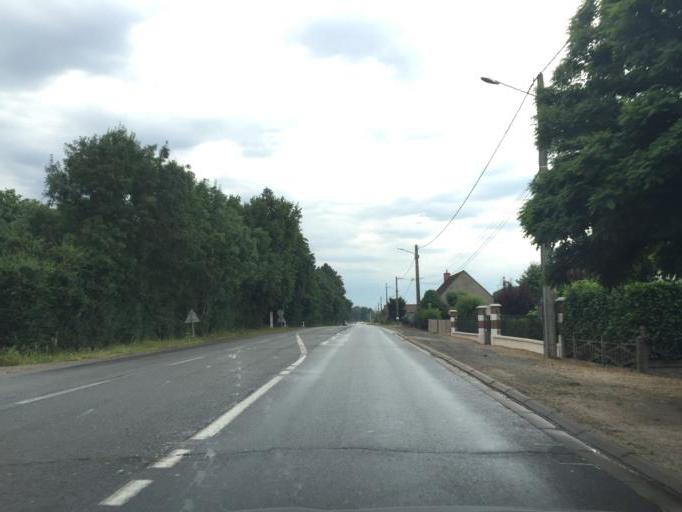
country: FR
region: Auvergne
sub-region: Departement de l'Allier
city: Varennes-sur-Allier
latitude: 46.3490
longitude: 3.3794
